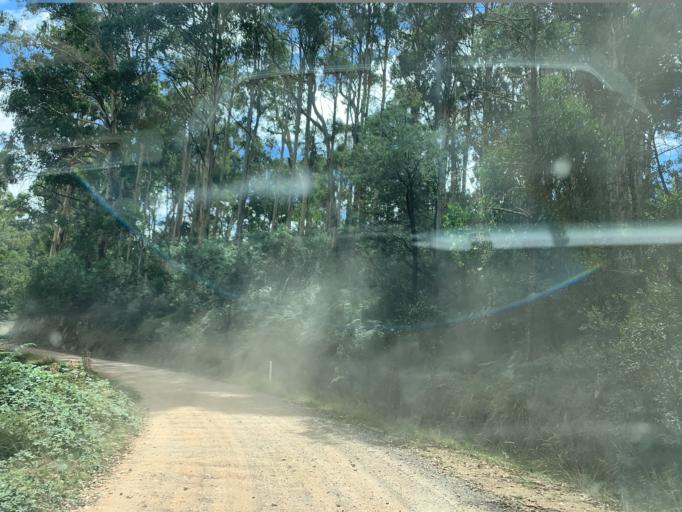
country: AU
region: Victoria
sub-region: Mansfield
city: Mansfield
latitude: -37.0980
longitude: 146.5135
